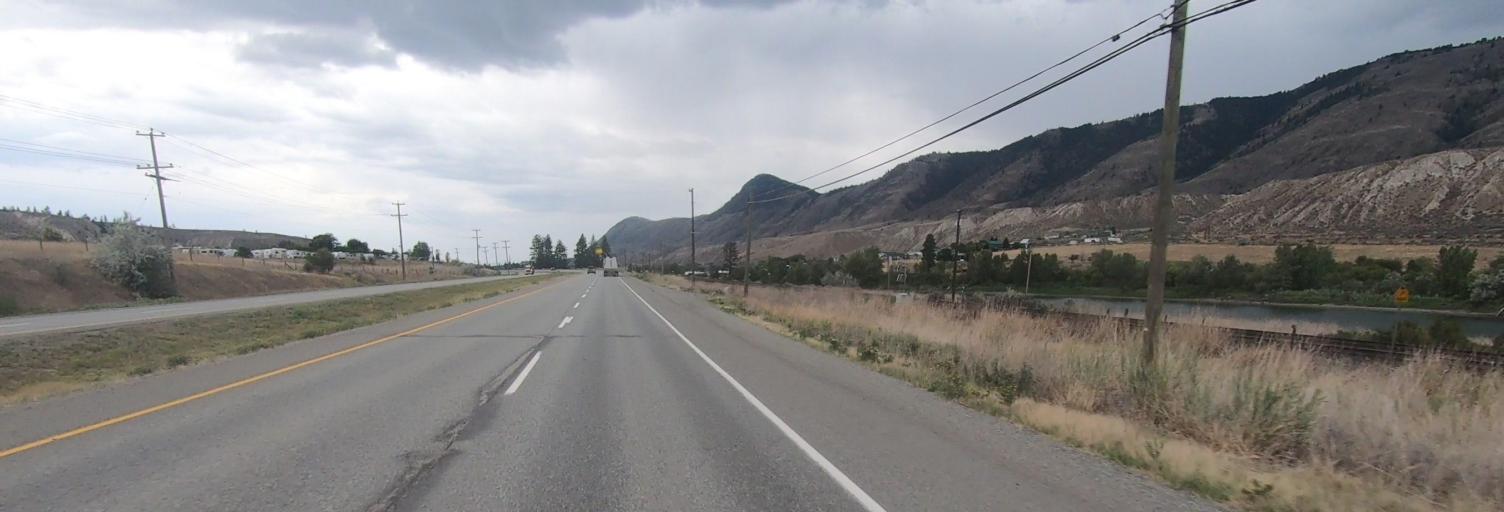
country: CA
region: British Columbia
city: Kamloops
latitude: 50.6709
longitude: -120.2084
